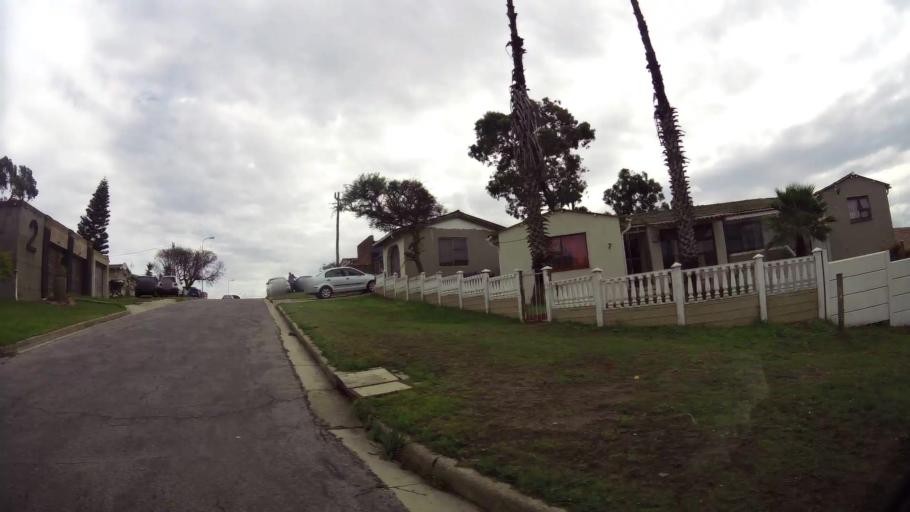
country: ZA
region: Eastern Cape
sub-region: Nelson Mandela Bay Metropolitan Municipality
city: Port Elizabeth
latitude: -33.9426
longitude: 25.5902
